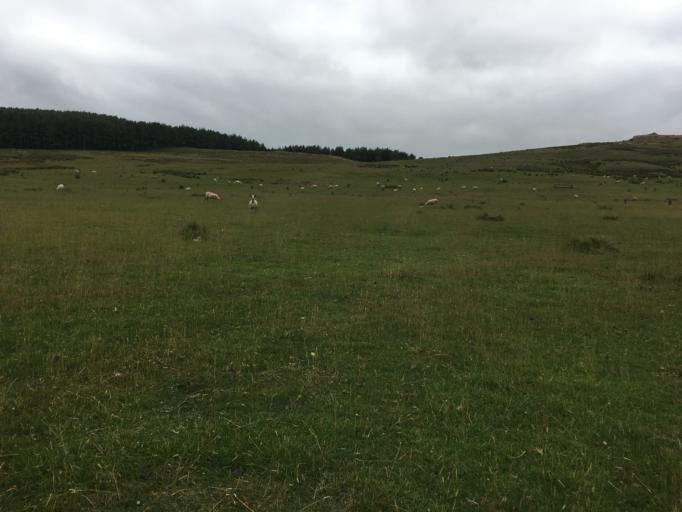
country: GB
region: England
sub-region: Northumberland
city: Belford
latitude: 55.6132
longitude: -1.9002
